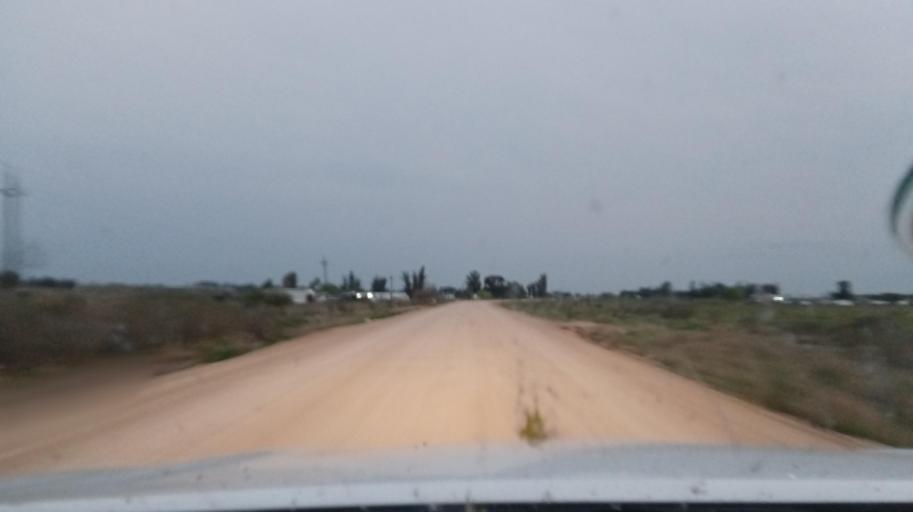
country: UY
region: Canelones
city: Santa Rosa
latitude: -34.5269
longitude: -56.0996
